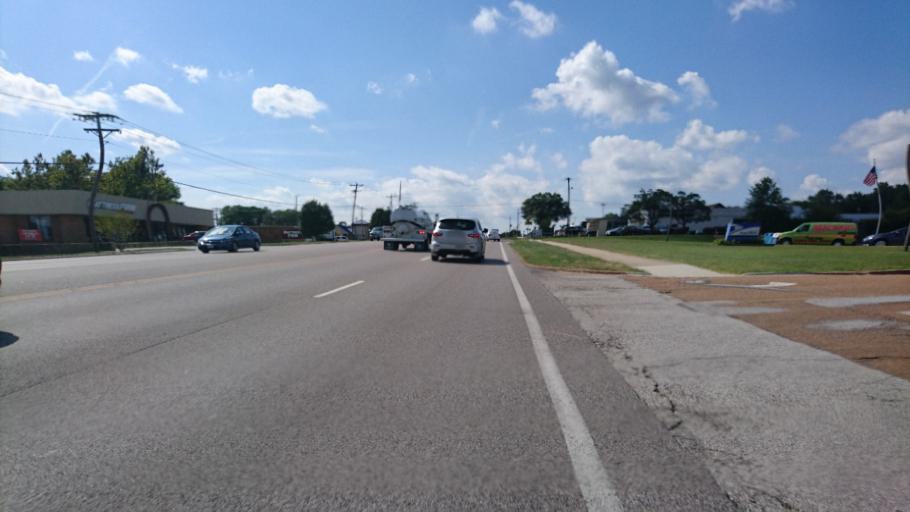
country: US
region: Missouri
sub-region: Saint Louis County
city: Ballwin
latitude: 38.5929
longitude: -90.5651
